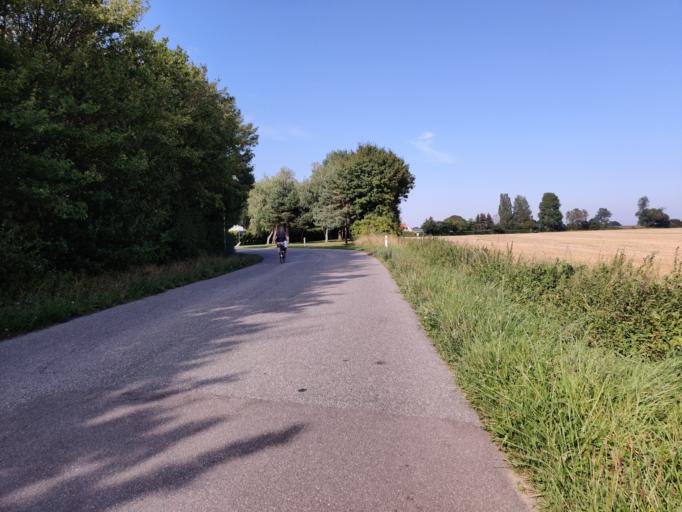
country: DK
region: Zealand
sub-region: Guldborgsund Kommune
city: Nykobing Falster
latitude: 54.7185
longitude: 11.9285
